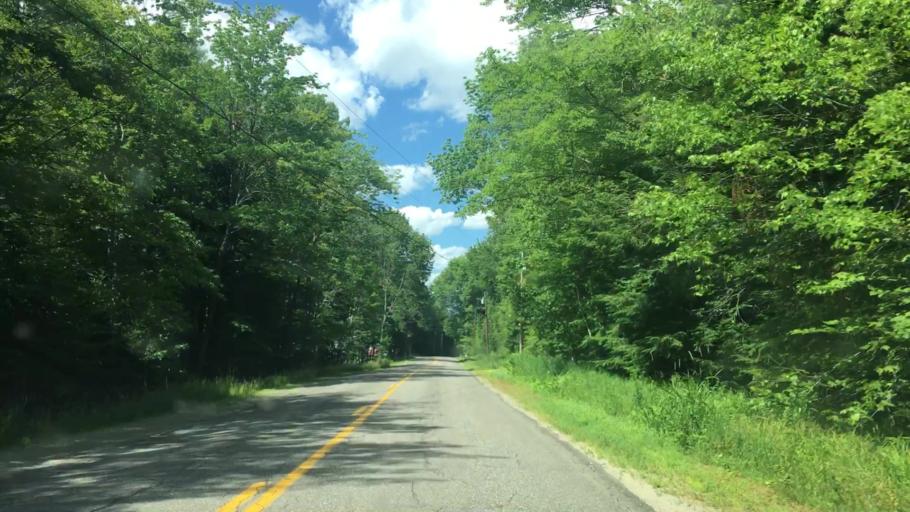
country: US
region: Maine
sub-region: Franklin County
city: Chesterville
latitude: 44.6085
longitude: -70.0829
